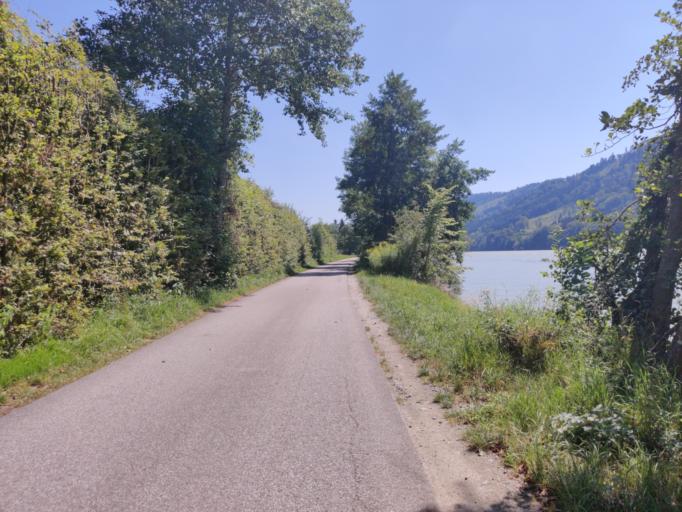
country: AT
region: Upper Austria
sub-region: Politischer Bezirk Rohrbach
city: Pfarrkirchen im Muehlkreis
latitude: 48.4551
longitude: 13.8217
